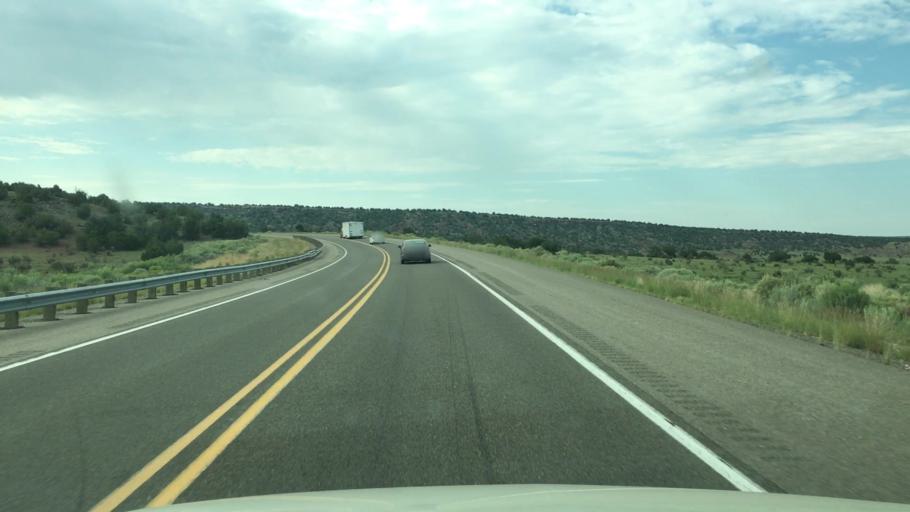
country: US
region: New Mexico
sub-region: Santa Fe County
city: Eldorado at Santa Fe
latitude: 35.2836
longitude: -105.8228
